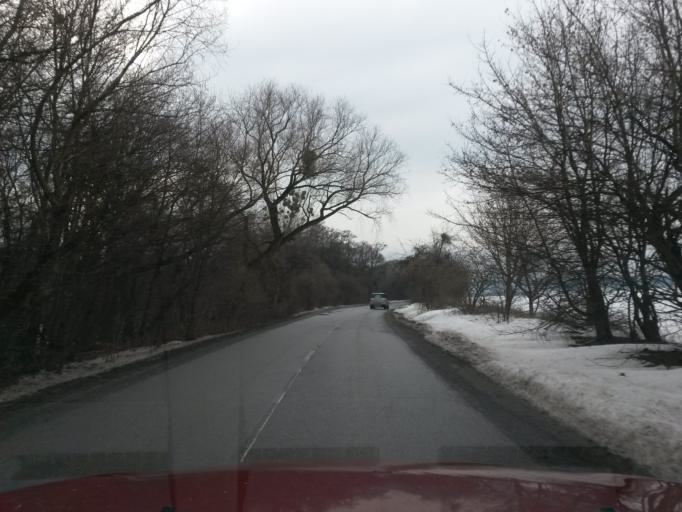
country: SK
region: Kosicky
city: Kosice
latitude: 48.7614
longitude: 21.3564
